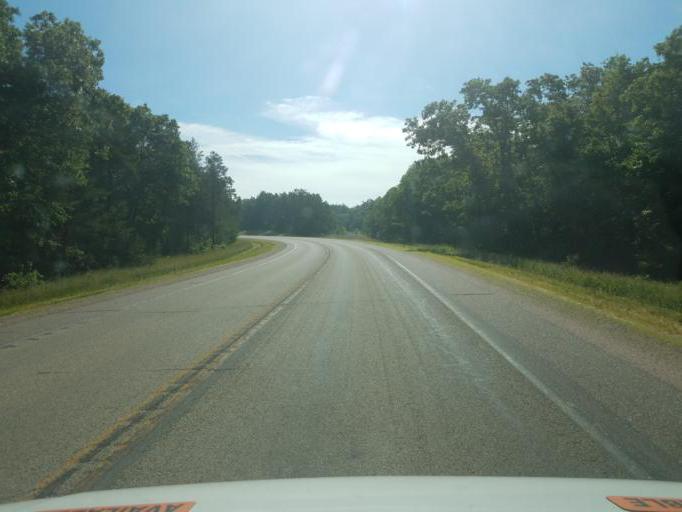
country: US
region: Wisconsin
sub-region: Sauk County
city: Lake Delton
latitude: 43.5687
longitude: -89.8287
